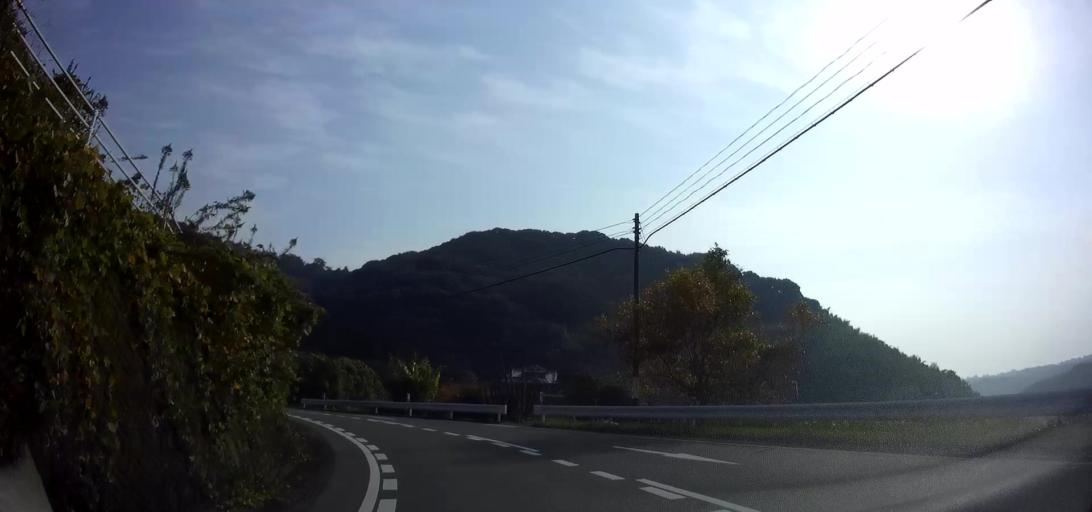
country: JP
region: Nagasaki
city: Shimabara
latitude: 32.6715
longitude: 130.2159
